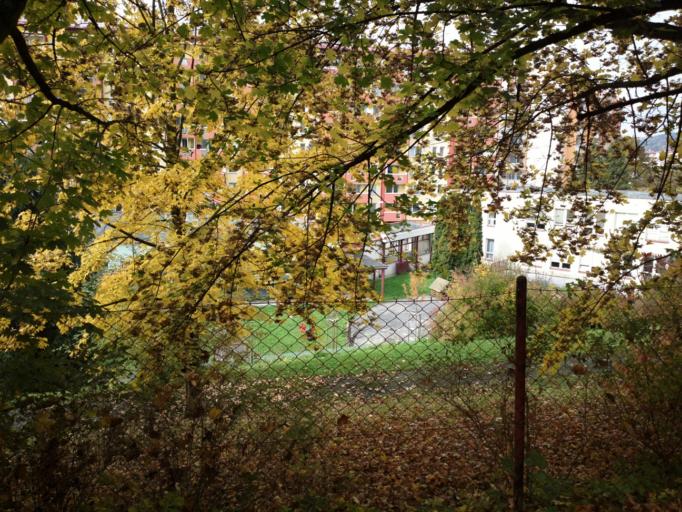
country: CZ
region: Zlin
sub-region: Okres Vsetin
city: Vsetin
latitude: 49.3307
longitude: 17.9879
